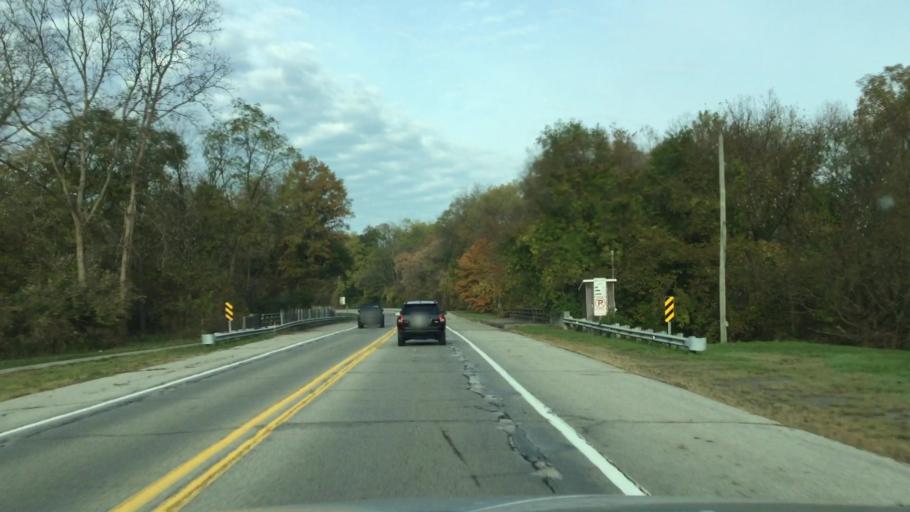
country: US
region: Michigan
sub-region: Wayne County
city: Dearborn Heights
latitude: 42.3305
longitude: -83.2472
